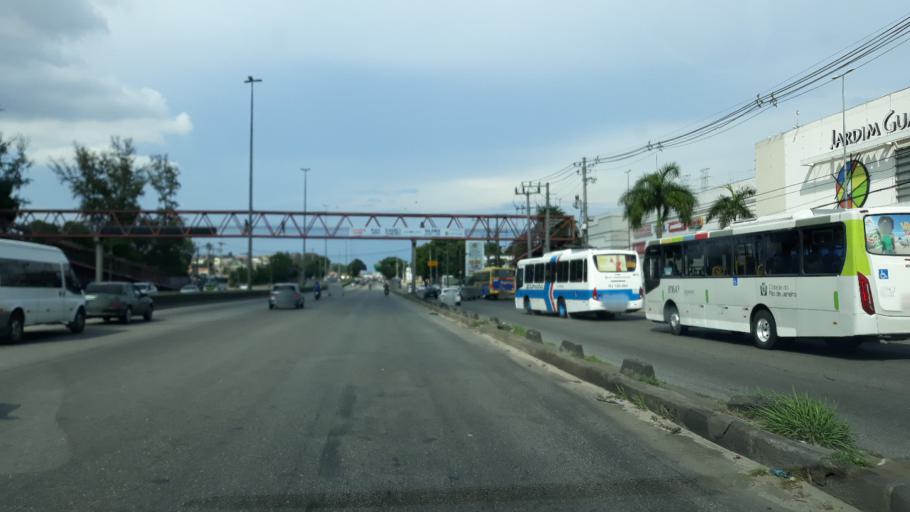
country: BR
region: Rio de Janeiro
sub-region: Sao Joao De Meriti
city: Sao Joao de Meriti
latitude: -22.8406
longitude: -43.3698
